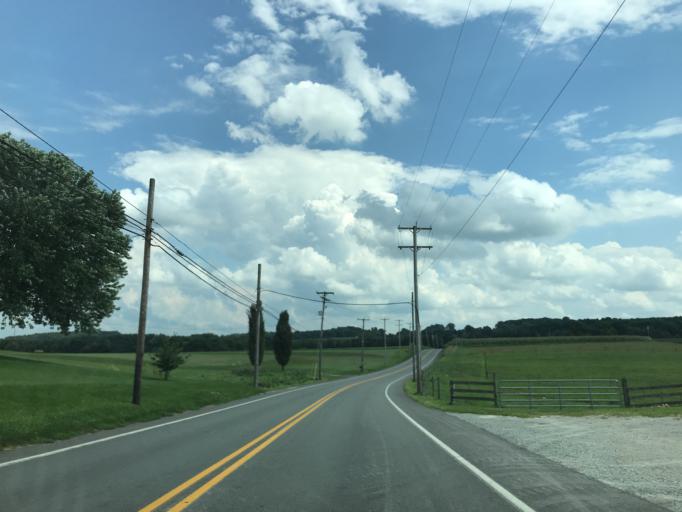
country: US
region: Pennsylvania
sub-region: York County
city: Windsor
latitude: 39.8781
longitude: -76.5150
